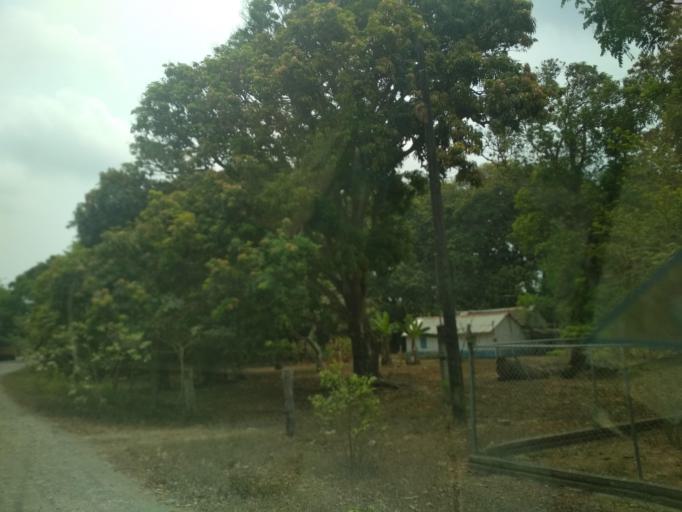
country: MX
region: Veracruz
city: Paso del Toro
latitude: 19.0394
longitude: -96.1528
